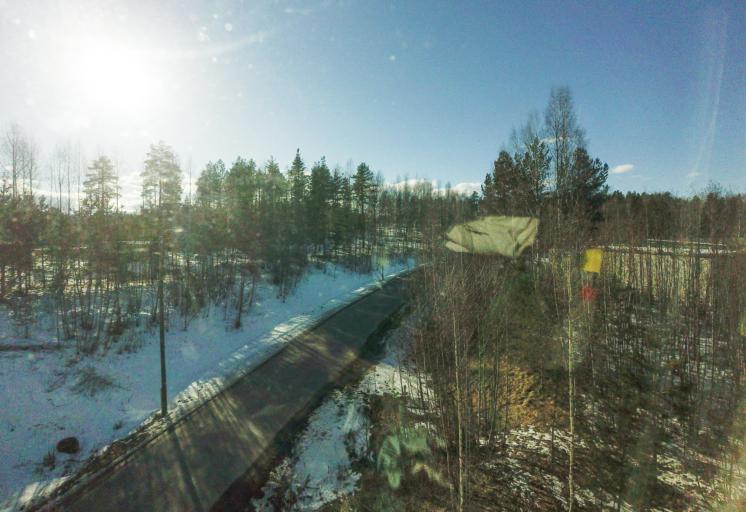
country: FI
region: South Karelia
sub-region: Imatra
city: Parikkala
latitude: 61.5411
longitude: 29.5201
